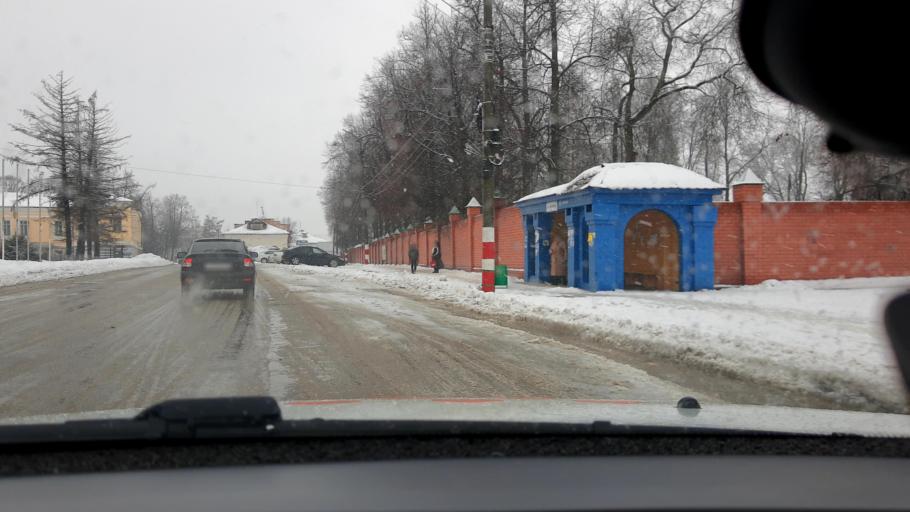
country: RU
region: Nizjnij Novgorod
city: Novaya Balakhna
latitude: 56.4916
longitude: 43.6134
